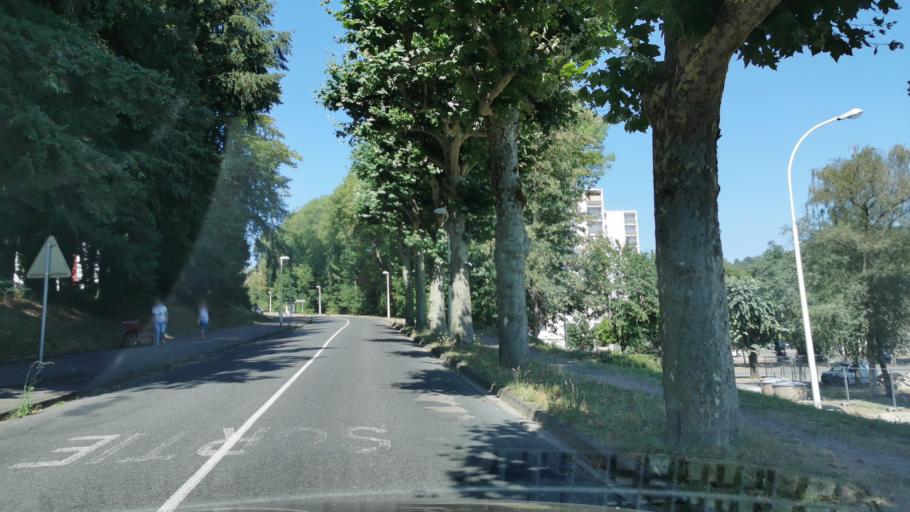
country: FR
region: Bourgogne
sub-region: Departement de Saone-et-Loire
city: Le Creusot
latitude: 46.8026
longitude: 4.4165
